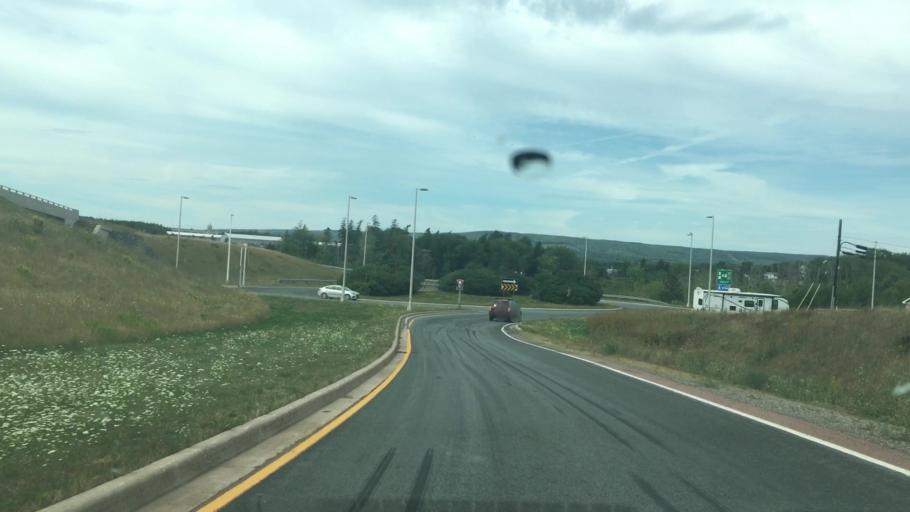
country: CA
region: Nova Scotia
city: Antigonish
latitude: 45.6121
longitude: -61.9979
